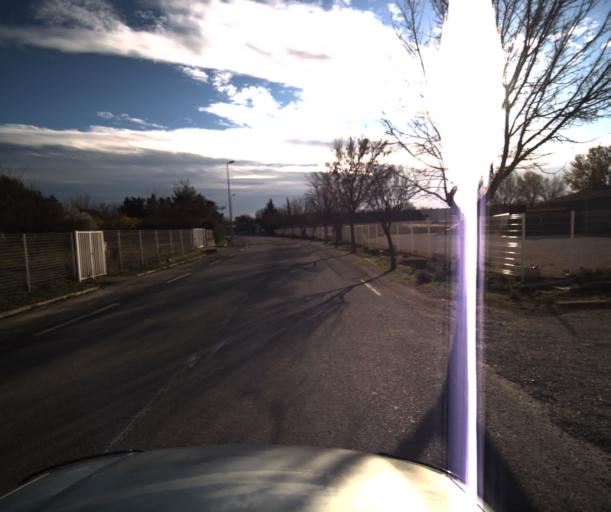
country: FR
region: Provence-Alpes-Cote d'Azur
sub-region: Departement du Vaucluse
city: Pertuis
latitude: 43.6761
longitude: 5.5029
